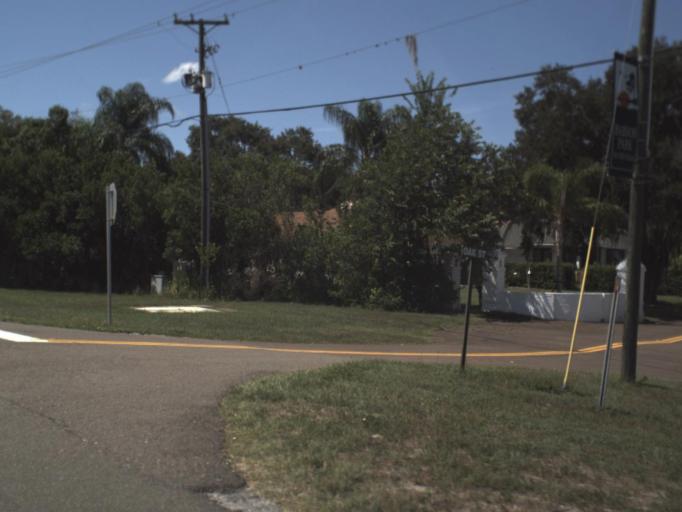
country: US
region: Florida
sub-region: Polk County
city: Babson Park
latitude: 27.8258
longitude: -81.5309
